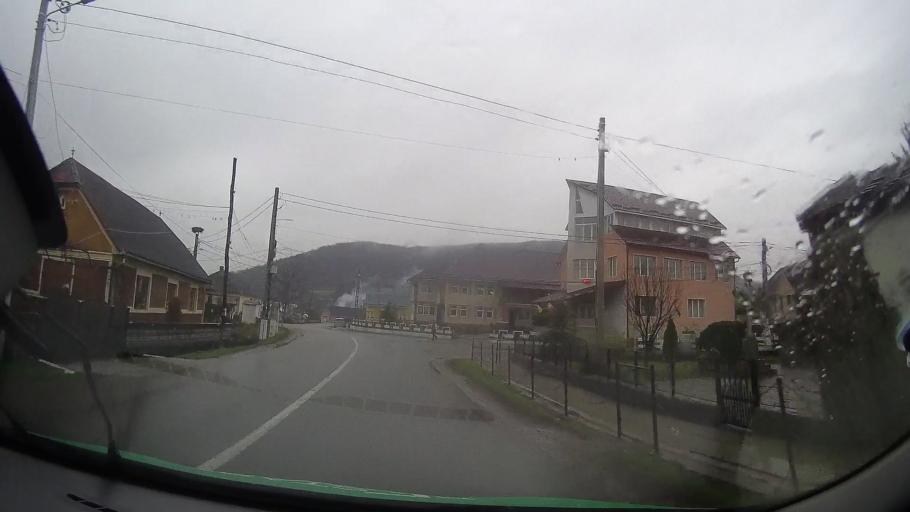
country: RO
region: Bistrita-Nasaud
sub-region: Comuna Sieut
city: Sieut
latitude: 46.9765
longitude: 24.6482
